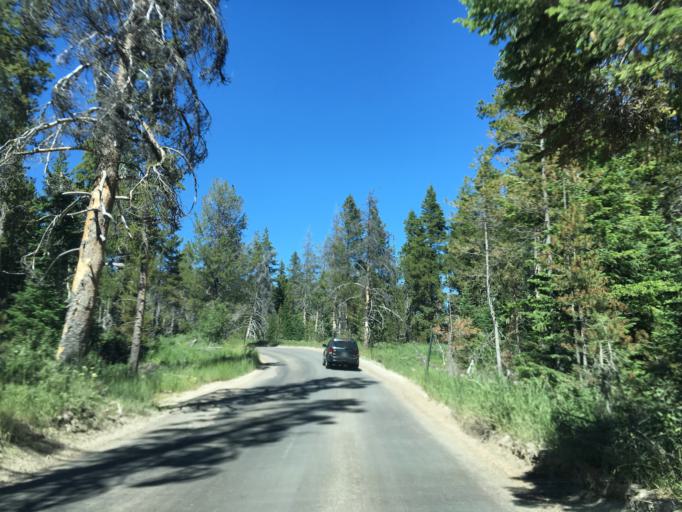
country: US
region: Wyoming
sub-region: Teton County
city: Moose Wilson Road
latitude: 43.6196
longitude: -110.7884
